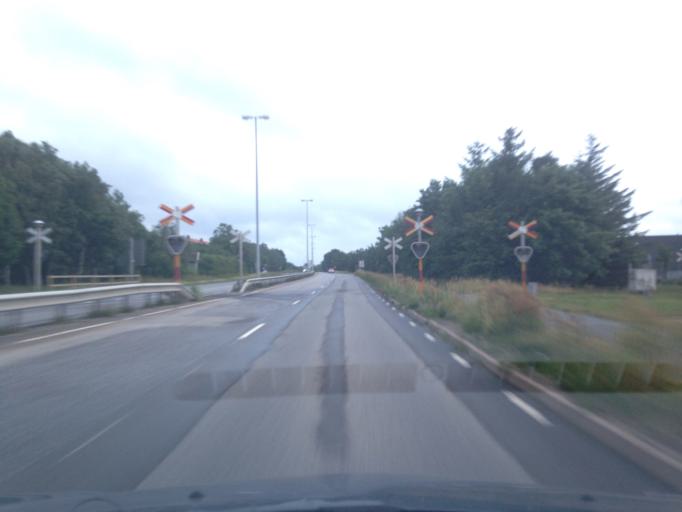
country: SE
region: Halland
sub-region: Varbergs Kommun
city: Varberg
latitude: 57.1210
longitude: 12.2618
